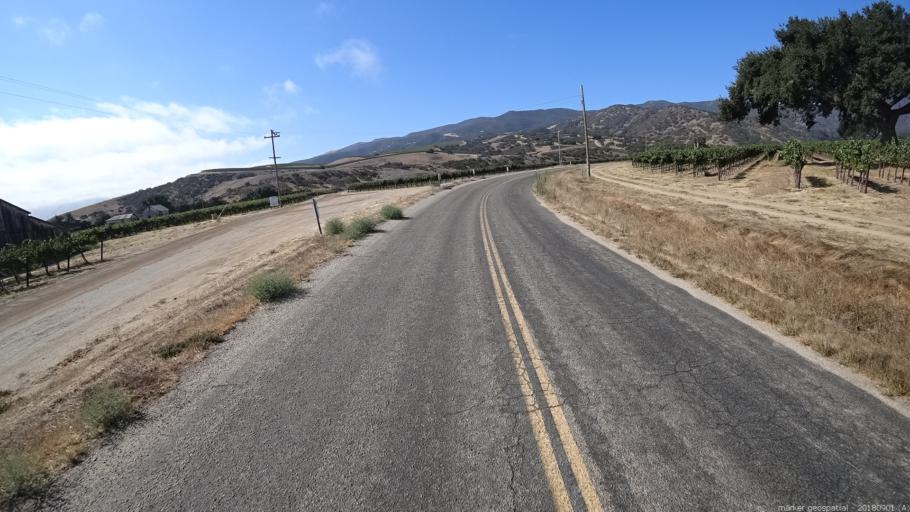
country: US
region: California
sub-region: Monterey County
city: Soledad
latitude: 36.3391
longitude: -121.3422
